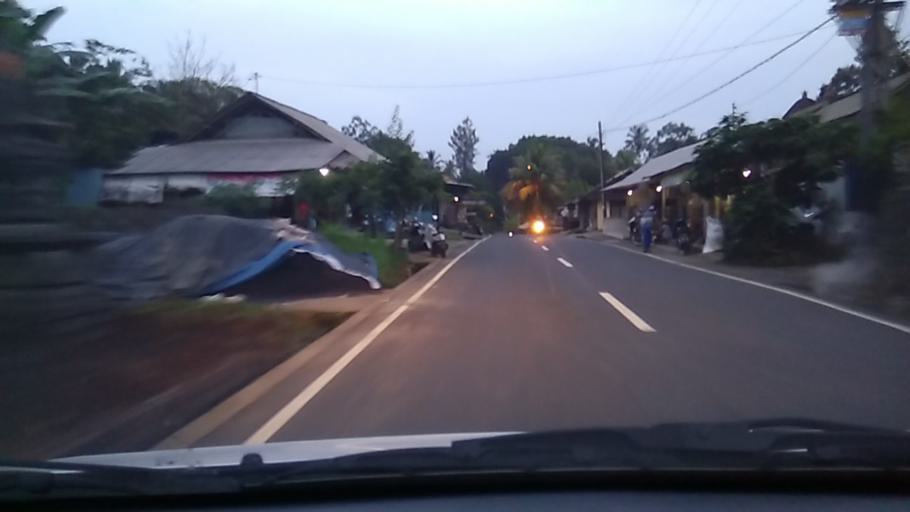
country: ID
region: Bali
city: Kekeran
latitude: -8.4730
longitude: 115.1913
